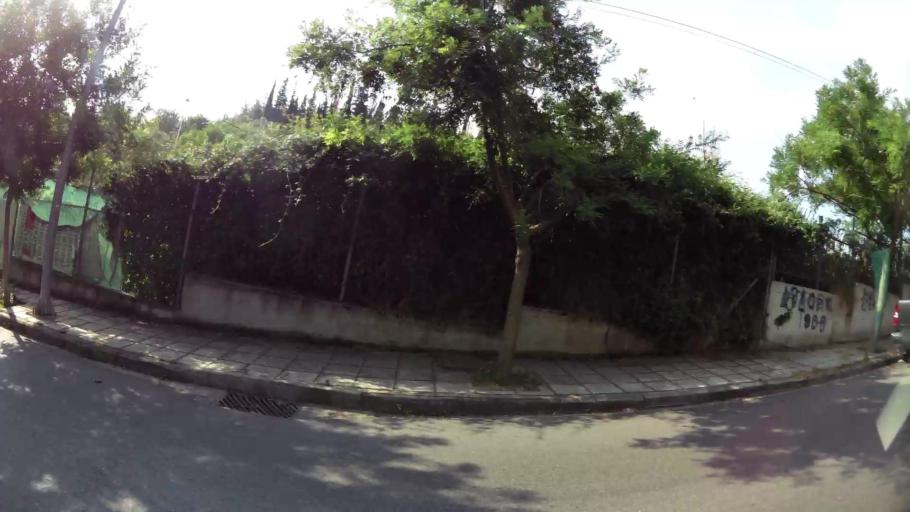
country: GR
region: Central Macedonia
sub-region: Nomos Thessalonikis
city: Sykies
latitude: 40.6525
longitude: 22.9607
